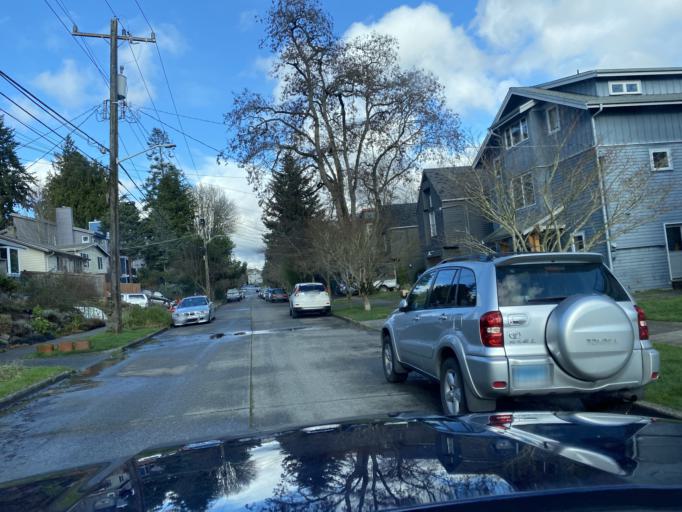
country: US
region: Washington
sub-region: King County
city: Seattle
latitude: 47.6227
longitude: -122.2998
